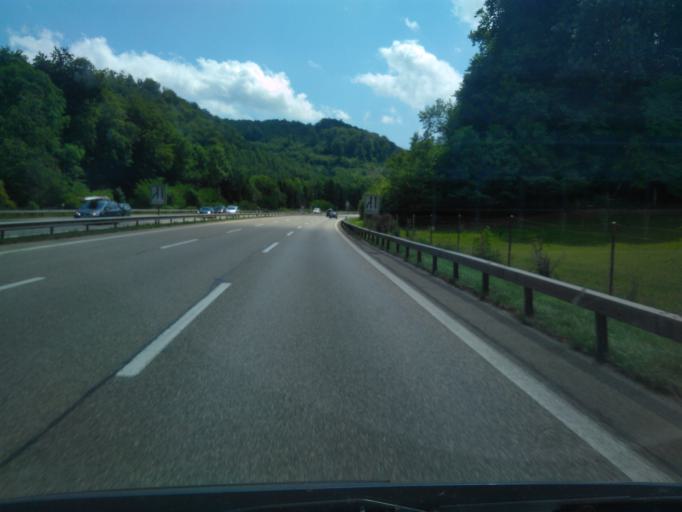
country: CH
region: Basel-Landschaft
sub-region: Bezirk Liestal
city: Arisdorf
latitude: 47.4962
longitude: 7.7673
